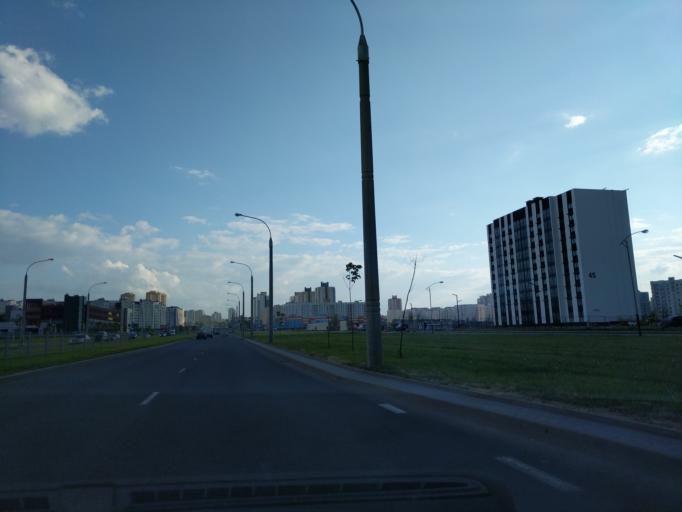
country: BY
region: Minsk
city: Zhdanovichy
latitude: 53.9303
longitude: 27.4451
